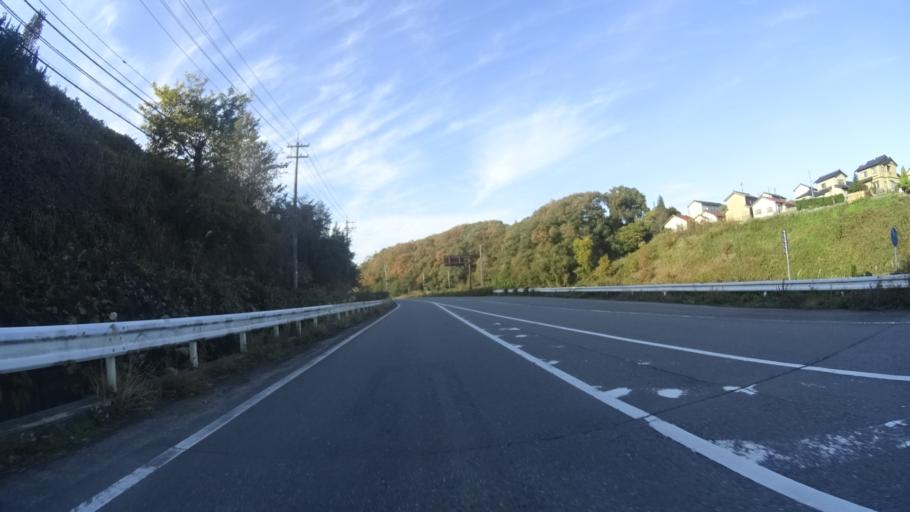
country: JP
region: Ishikawa
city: Hakui
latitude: 37.0233
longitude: 136.7859
